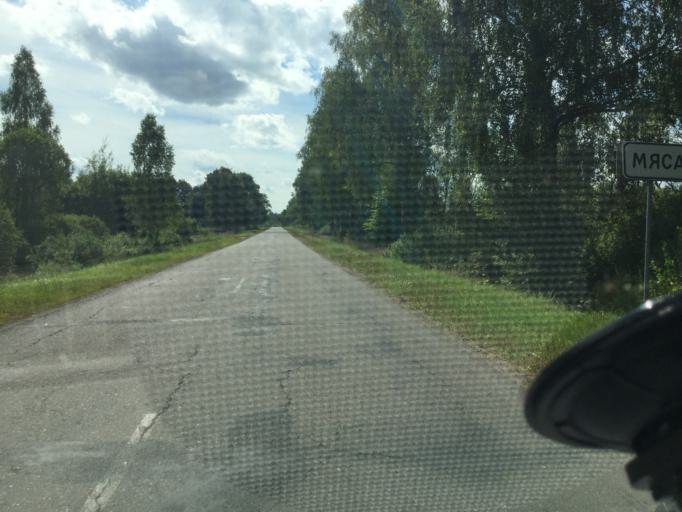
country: BY
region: Vitebsk
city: Chashniki
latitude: 55.2921
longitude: 29.3673
